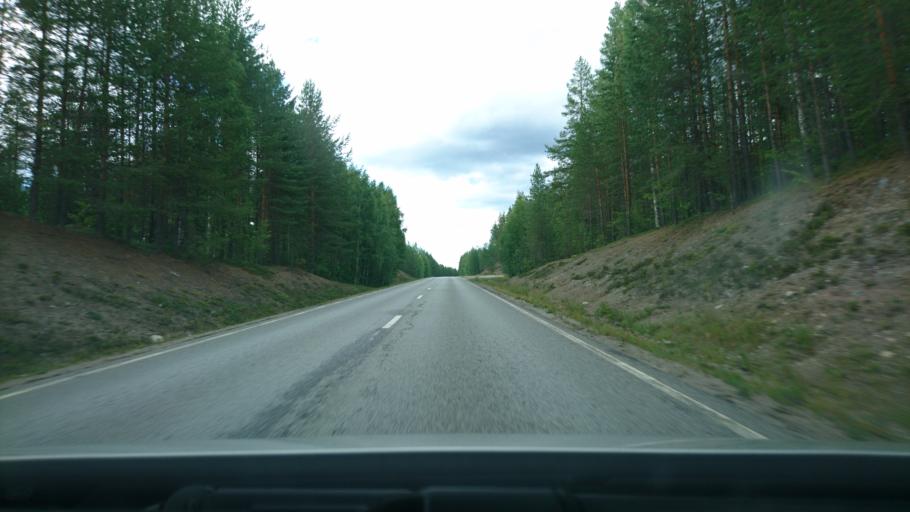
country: SE
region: Vaesterbotten
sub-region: Asele Kommun
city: Asele
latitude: 63.8794
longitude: 17.2048
